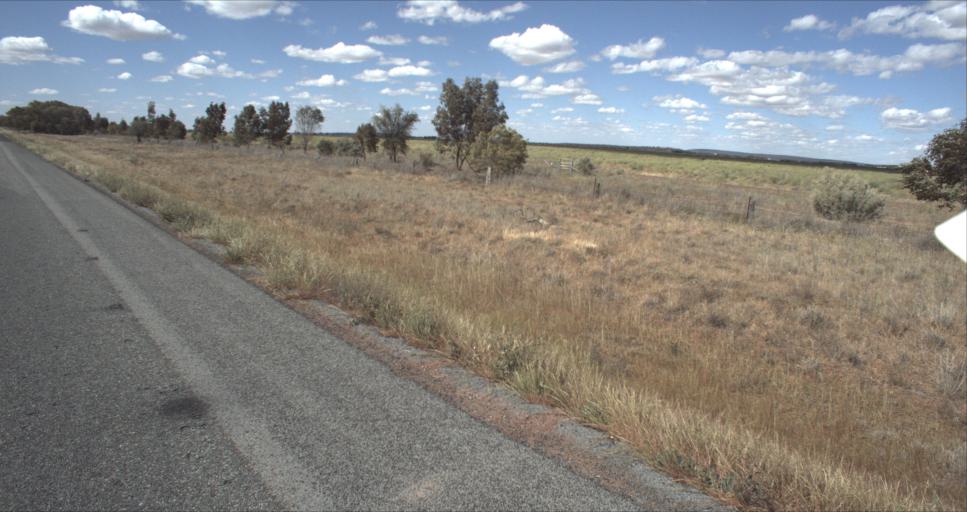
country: AU
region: New South Wales
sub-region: Leeton
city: Leeton
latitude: -34.4398
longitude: 146.2566
